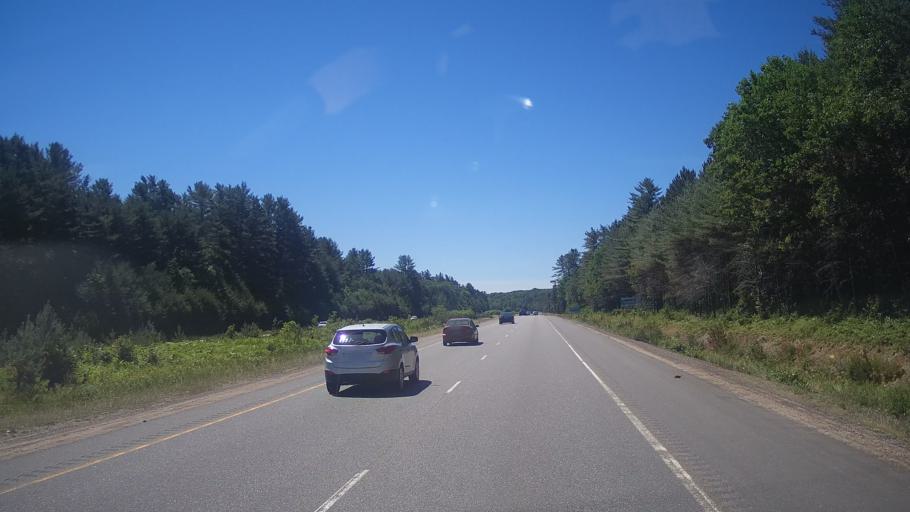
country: CA
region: Ontario
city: Bracebridge
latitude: 45.1149
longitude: -79.3110
